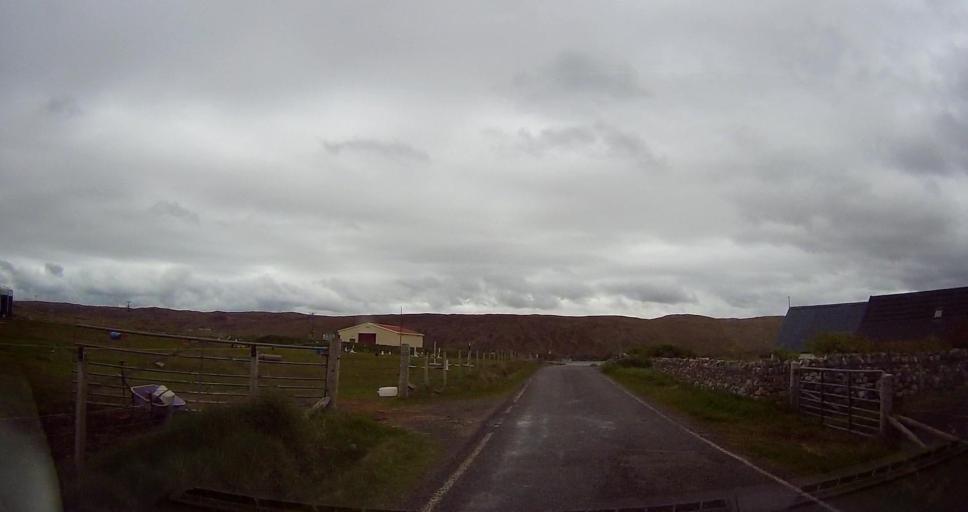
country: GB
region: Scotland
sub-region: Shetland Islands
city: Lerwick
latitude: 60.4843
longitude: -1.4787
